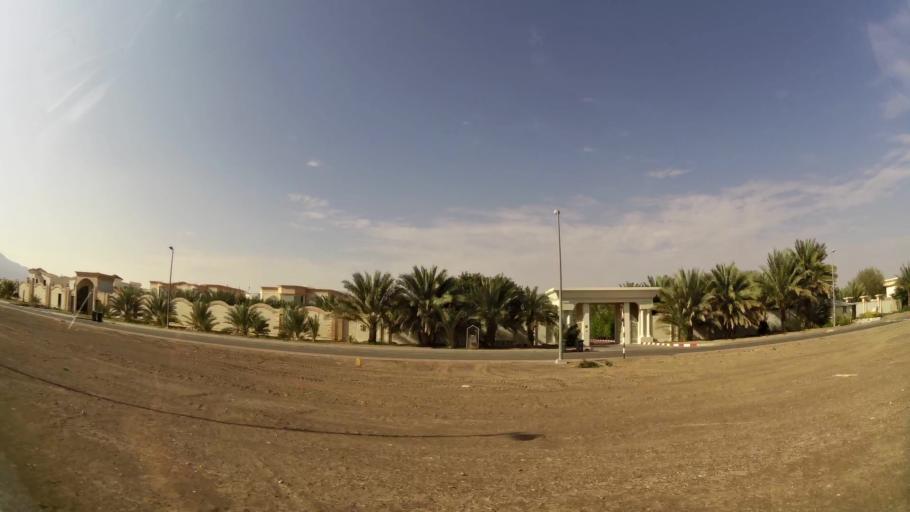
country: AE
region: Abu Dhabi
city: Al Ain
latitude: 24.0660
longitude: 55.8458
